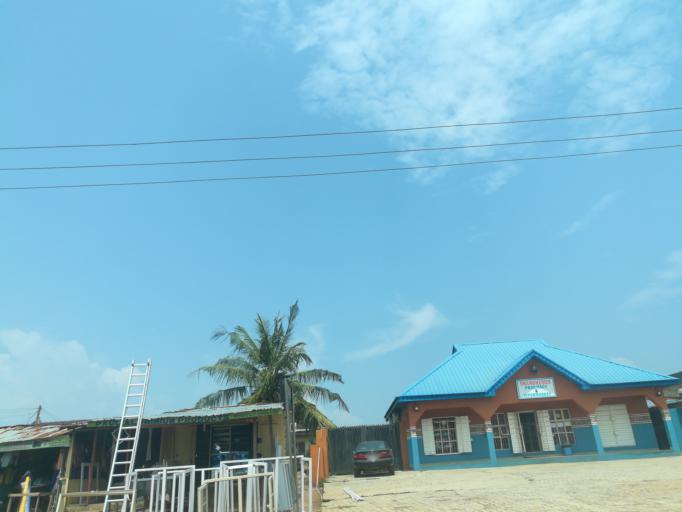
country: NG
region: Lagos
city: Ikorodu
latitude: 6.5816
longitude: 3.6263
